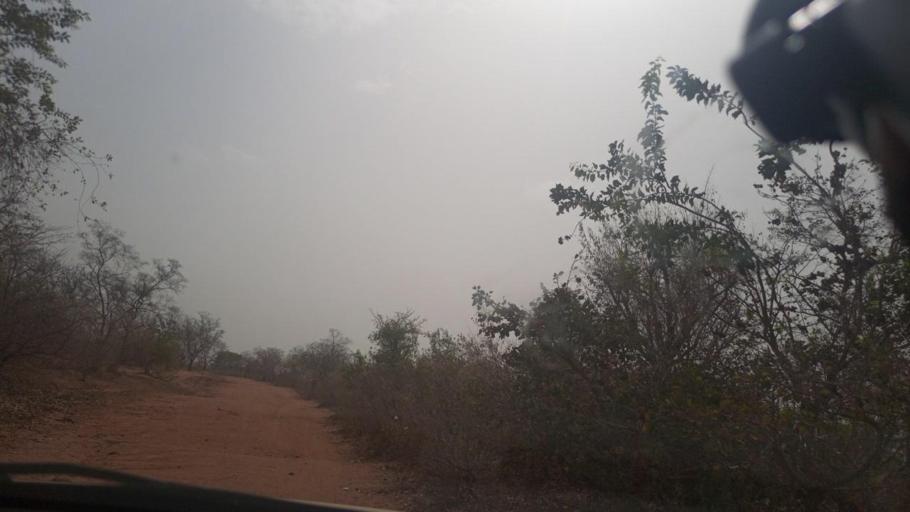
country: BF
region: Boucle du Mouhoun
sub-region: Province des Banwa
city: Salanso
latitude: 12.1882
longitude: -4.2161
